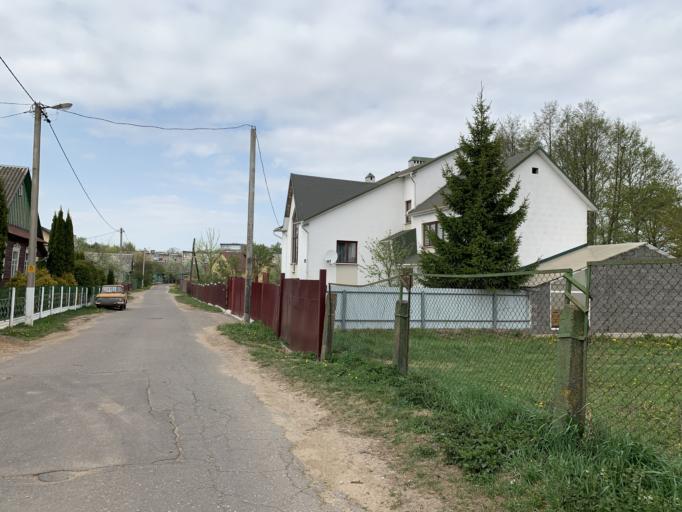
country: BY
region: Minsk
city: Nyasvizh
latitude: 53.2159
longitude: 26.6784
